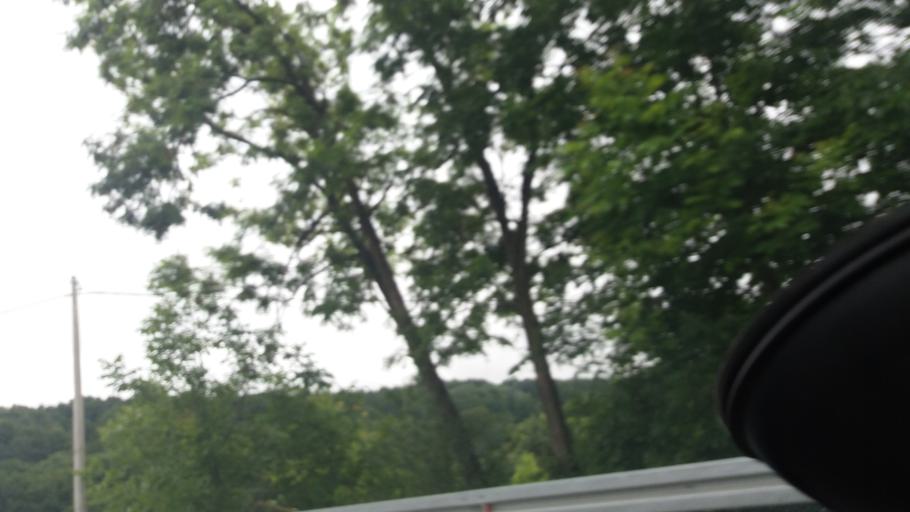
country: RS
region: Central Serbia
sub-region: Kolubarski Okrug
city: Ljig
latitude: 44.2214
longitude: 20.1679
